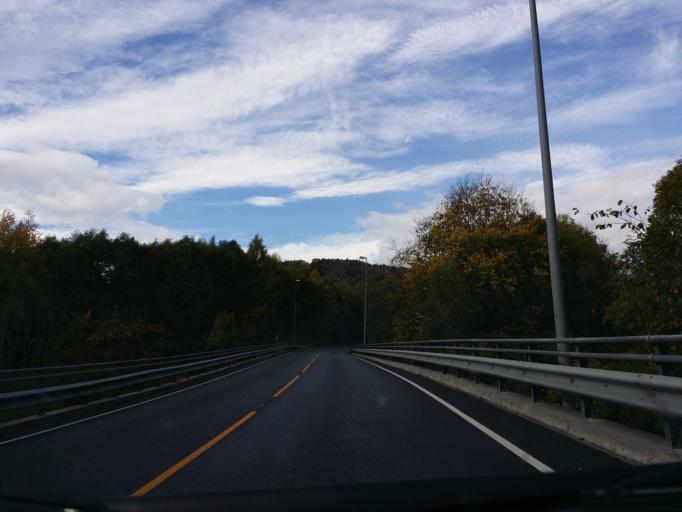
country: NO
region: Akershus
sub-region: Baerum
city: Sandvika
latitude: 59.9273
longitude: 10.4966
